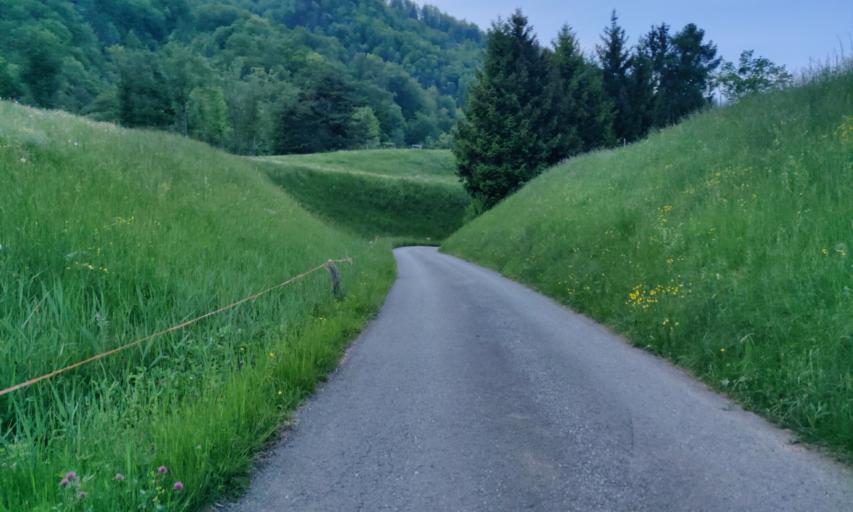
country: CH
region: Saint Gallen
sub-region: Wahlkreis Sarganserland
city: Sargans
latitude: 47.0733
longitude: 9.4607
